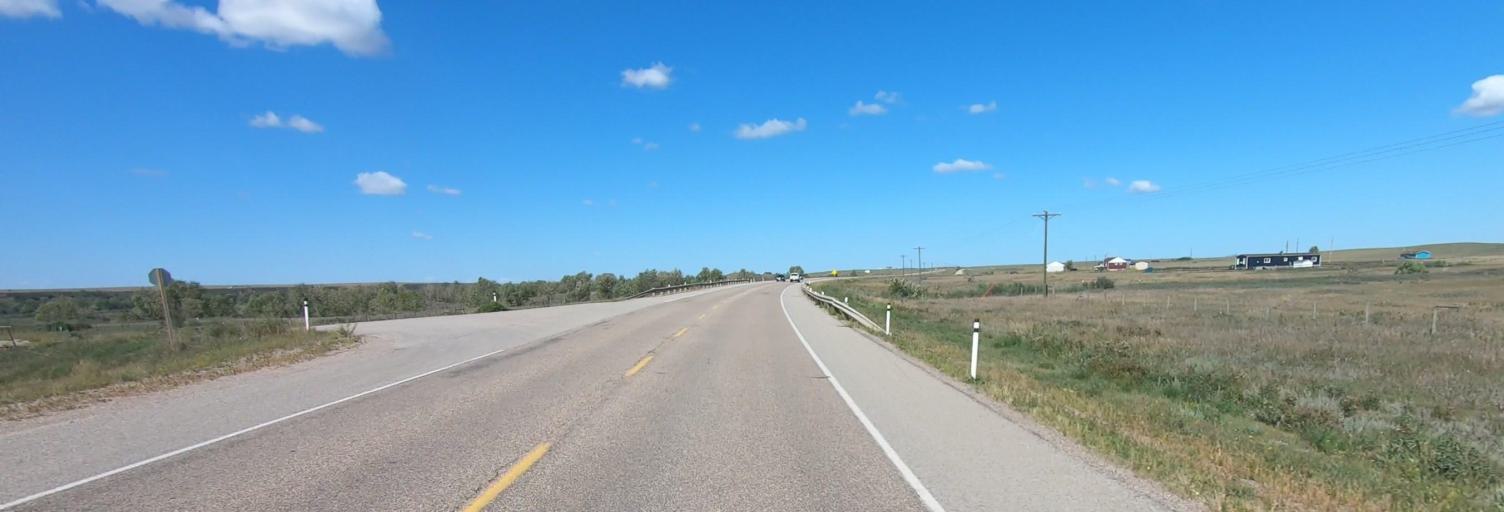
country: CA
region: Alberta
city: Strathmore
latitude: 50.8564
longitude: -113.1326
